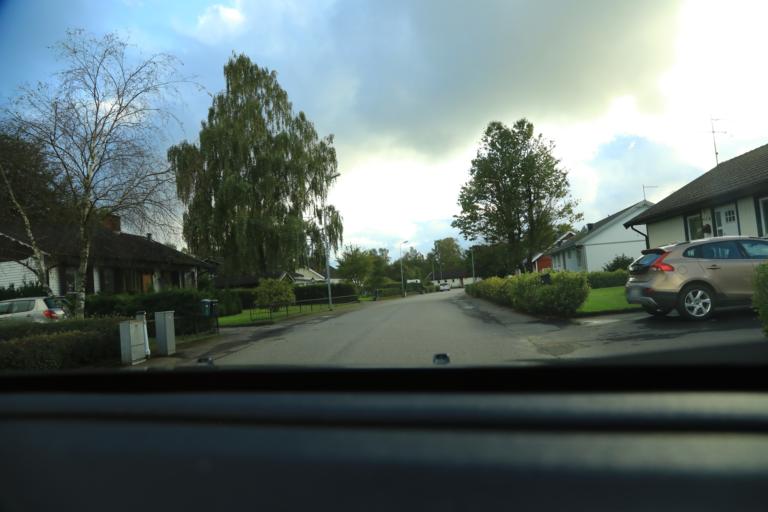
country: SE
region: Halland
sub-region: Halmstads Kommun
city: Getinge
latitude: 57.1298
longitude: 12.7137
